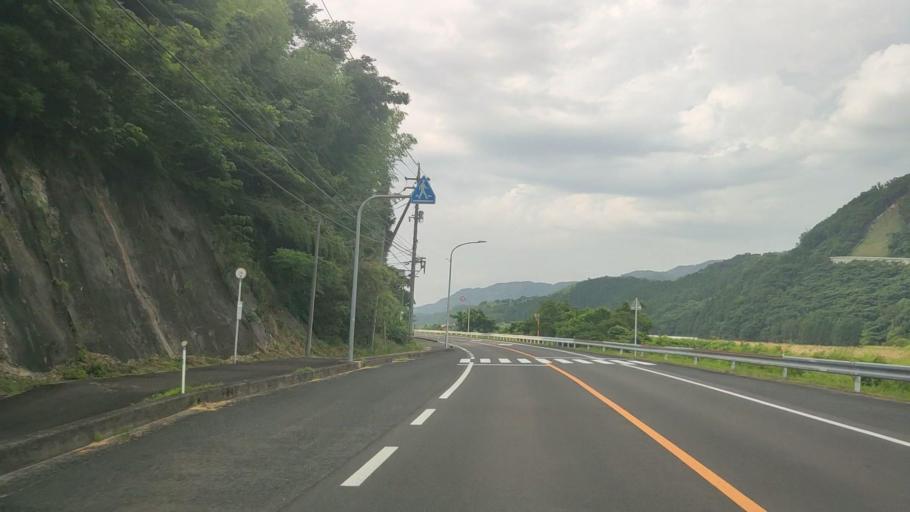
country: JP
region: Tottori
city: Kurayoshi
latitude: 35.3414
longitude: 133.8407
